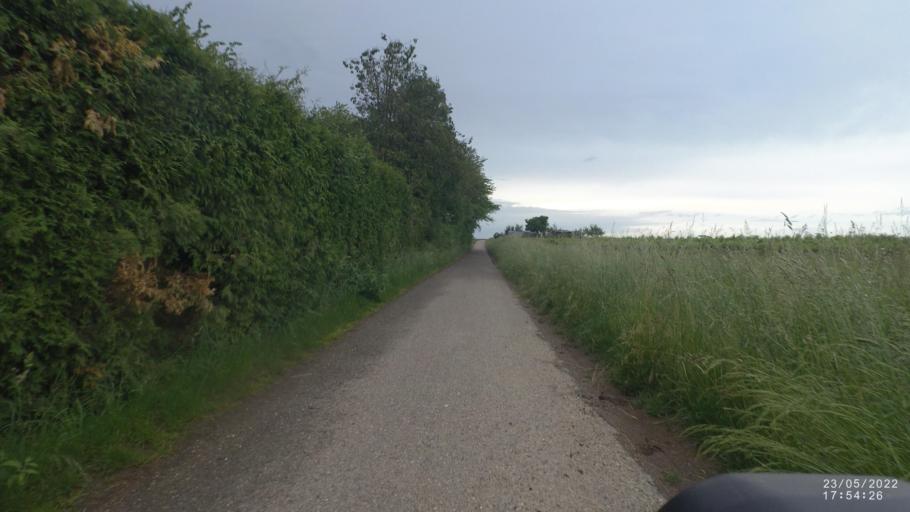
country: DE
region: Baden-Wuerttemberg
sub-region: Regierungsbezirk Stuttgart
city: Waiblingen
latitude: 48.8384
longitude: 9.2875
